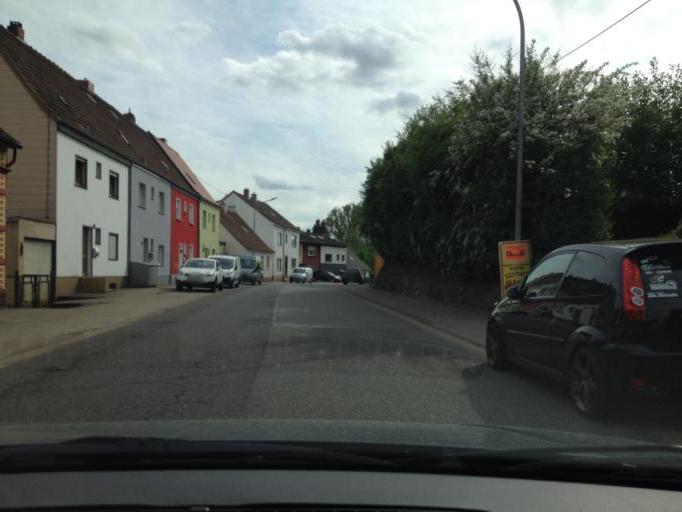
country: DE
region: Saarland
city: Hangard
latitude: 49.3741
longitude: 7.1927
